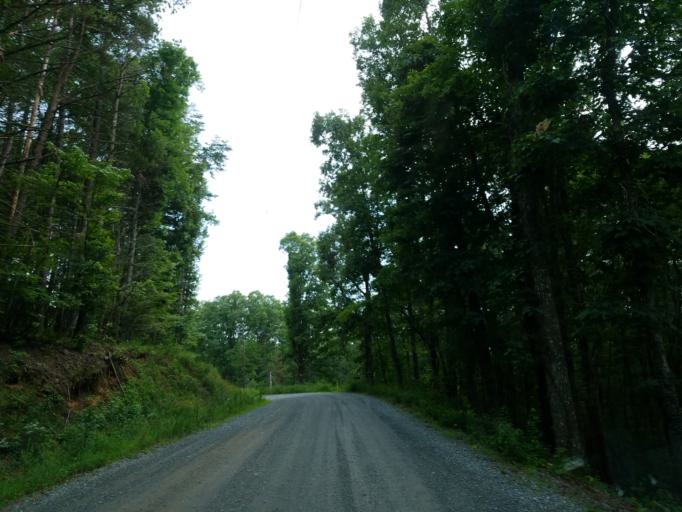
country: US
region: Georgia
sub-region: Fannin County
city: Blue Ridge
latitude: 34.8313
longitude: -84.2310
